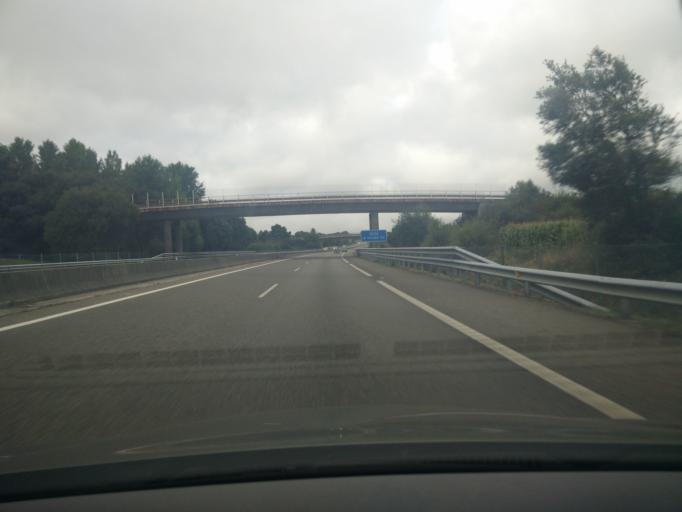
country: ES
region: Galicia
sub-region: Provincia da Coruna
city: Laracha
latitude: 43.2608
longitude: -8.5972
